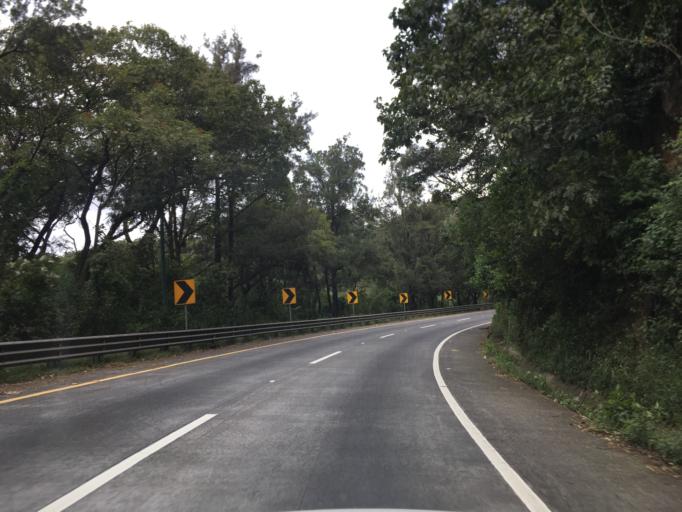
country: GT
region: Sacatepequez
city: Santa Lucia Milpas Altas
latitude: 14.5663
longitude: -90.6882
